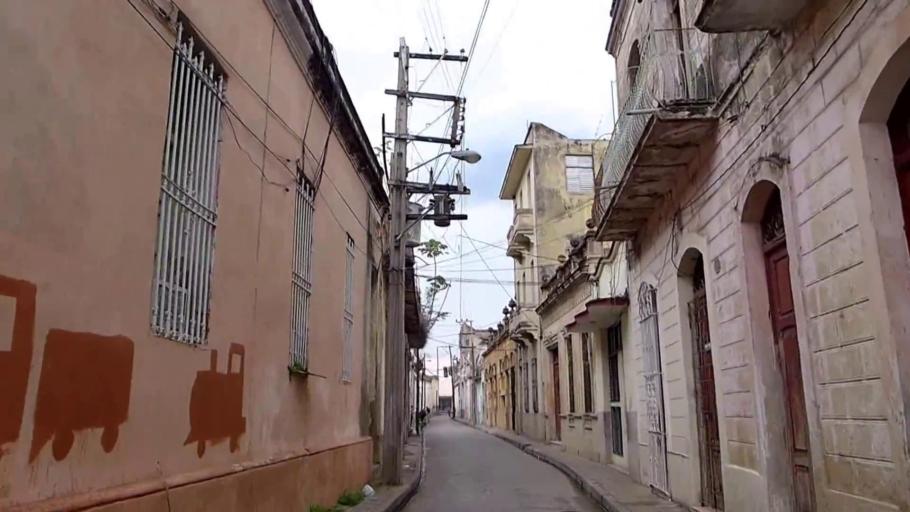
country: CU
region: Camaguey
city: Camaguey
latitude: 21.3803
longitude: -77.9176
